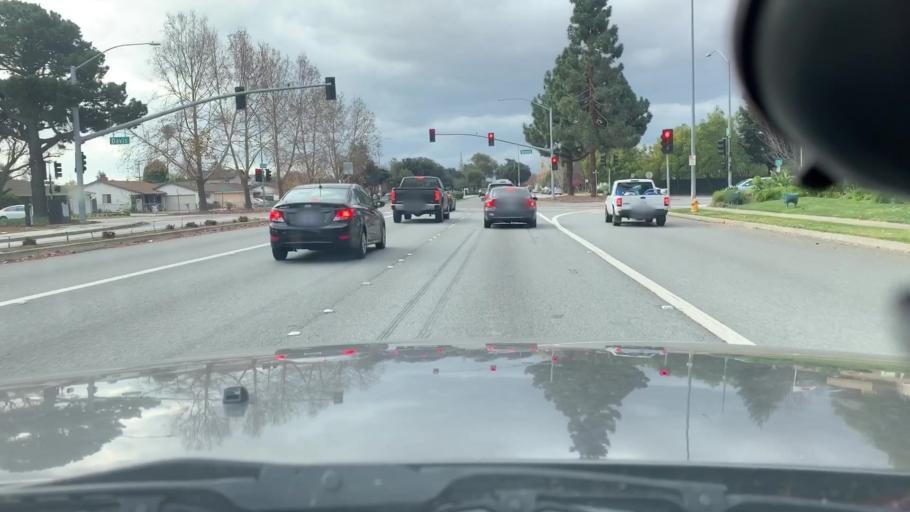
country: US
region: California
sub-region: Alameda County
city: Fremont
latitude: 37.5376
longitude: -121.9756
